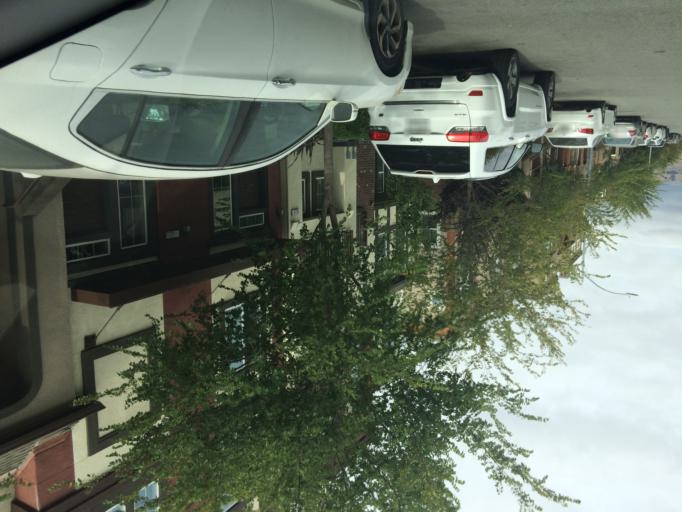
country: US
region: California
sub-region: Santa Clara County
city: San Jose
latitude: 37.3718
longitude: -121.8819
